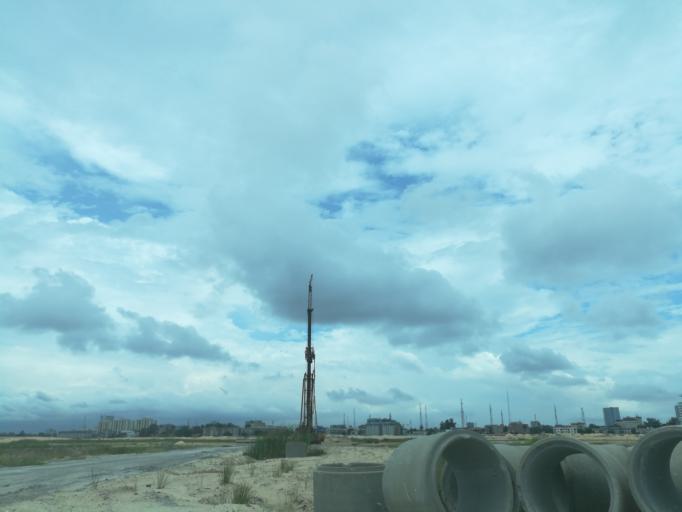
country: NG
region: Lagos
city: Ikoyi
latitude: 6.4157
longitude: 3.4219
